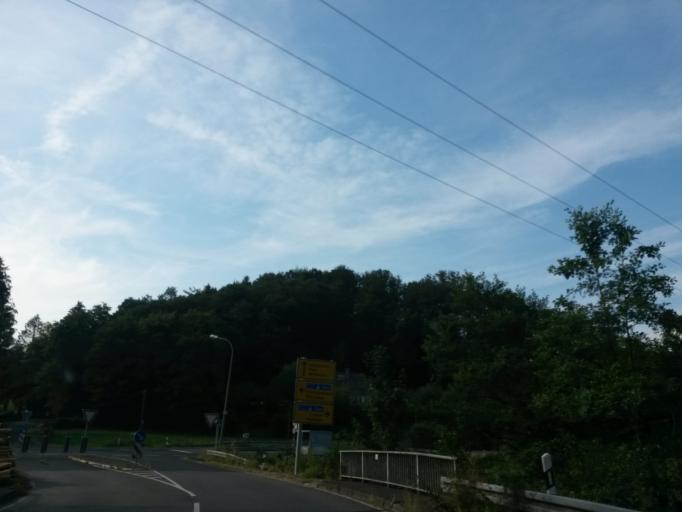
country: DE
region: North Rhine-Westphalia
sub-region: Regierungsbezirk Koln
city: Overath
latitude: 50.9838
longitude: 7.3022
